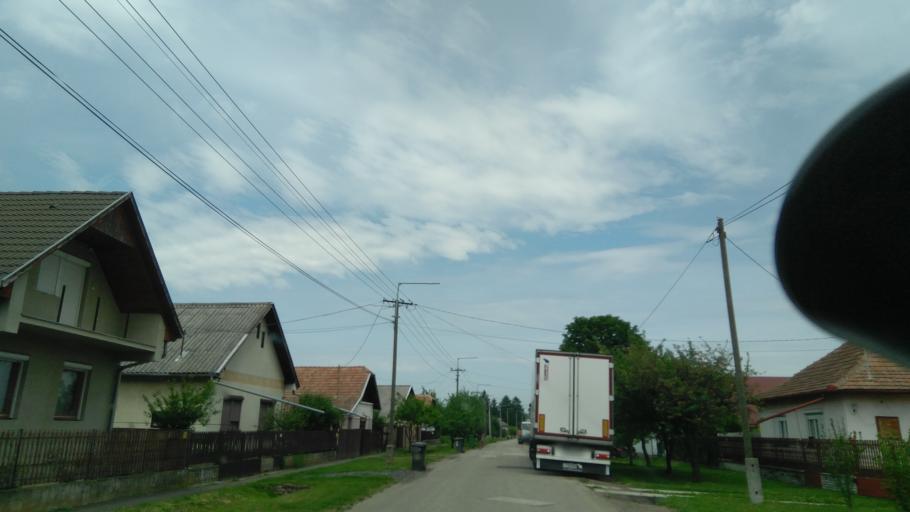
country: HU
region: Bekes
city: Fuzesgyarmat
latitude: 47.1029
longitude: 21.2055
